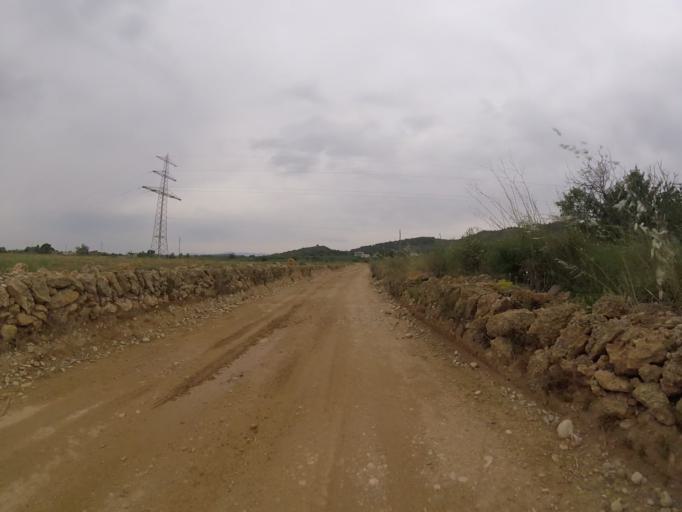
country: ES
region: Valencia
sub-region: Provincia de Castello
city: Alcoceber
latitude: 40.2439
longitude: 0.2605
